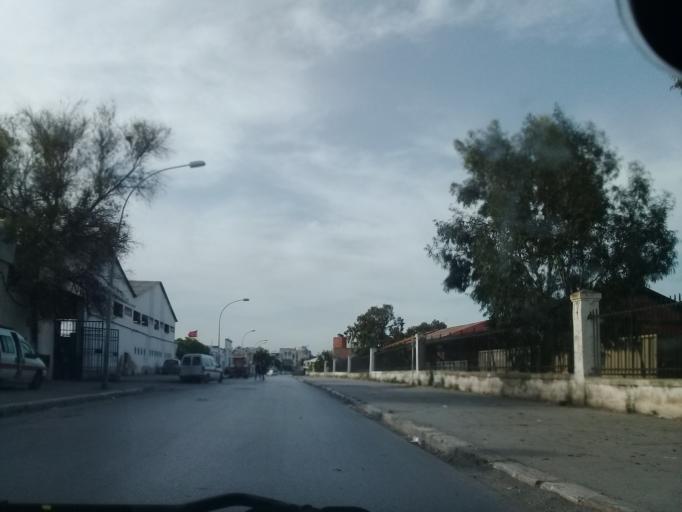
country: TN
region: Tunis
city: Tunis
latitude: 36.7911
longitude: 10.1879
